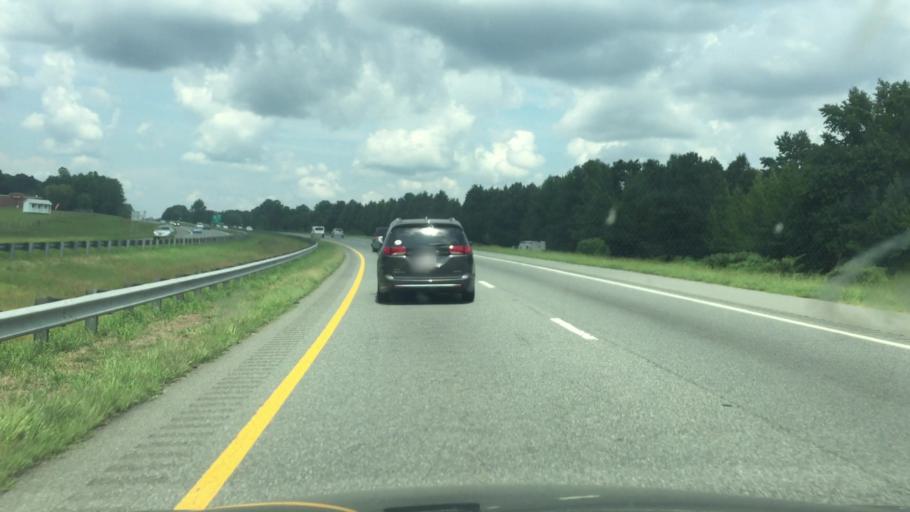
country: US
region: North Carolina
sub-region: Randolph County
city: Asheboro
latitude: 35.6125
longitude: -79.8194
